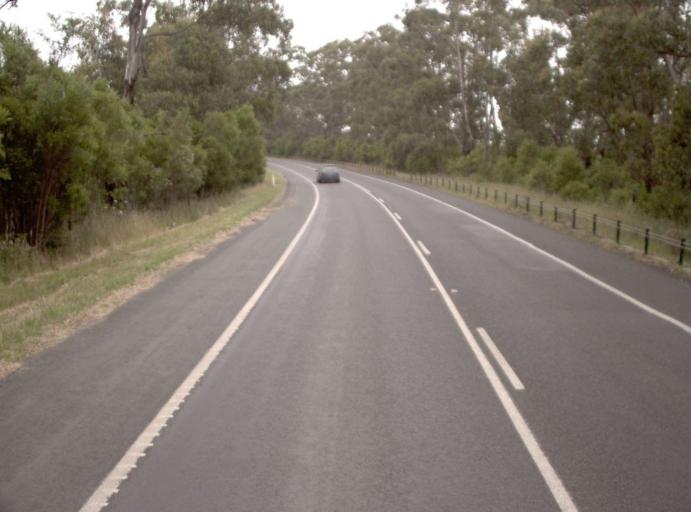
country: AU
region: Victoria
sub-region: Latrobe
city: Moe
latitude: -38.3004
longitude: 146.2820
